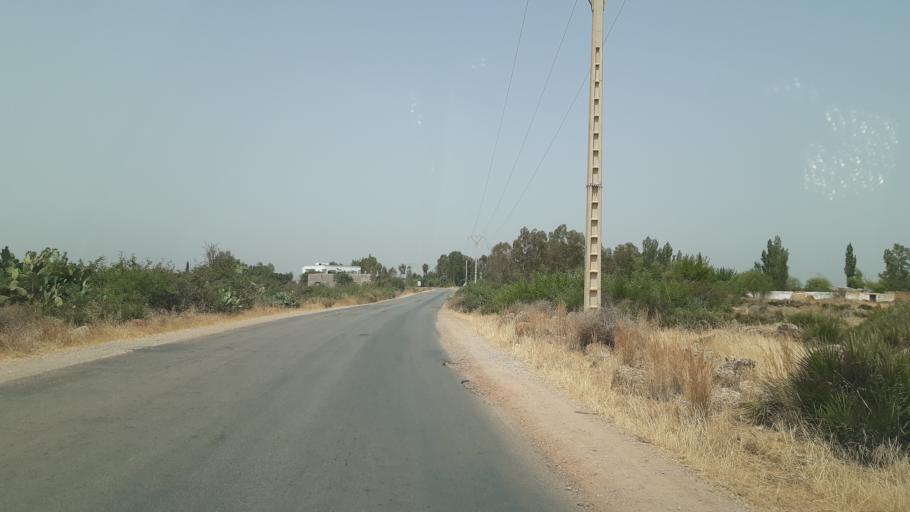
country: MA
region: Fes-Boulemane
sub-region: Fes
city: Oulad Tayeb
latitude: 33.8355
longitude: -5.1399
